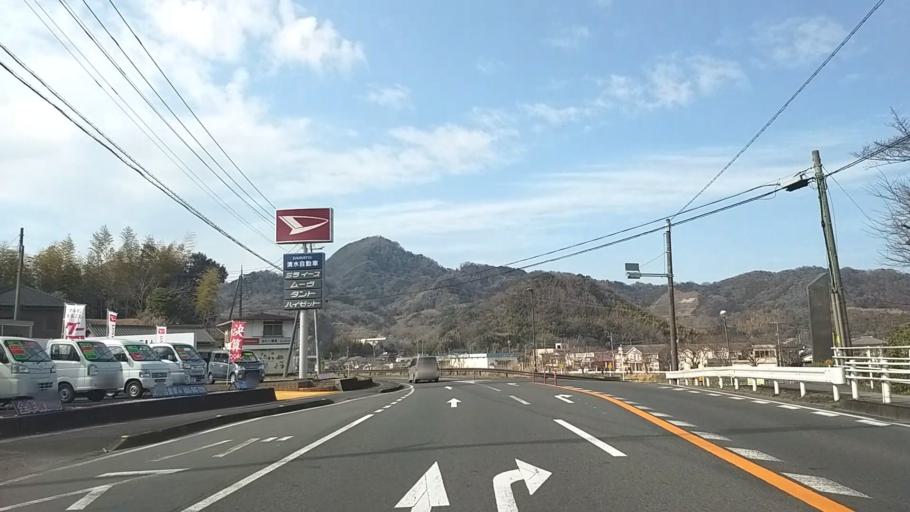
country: JP
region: Shizuoka
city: Mishima
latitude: 35.0451
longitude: 138.9189
